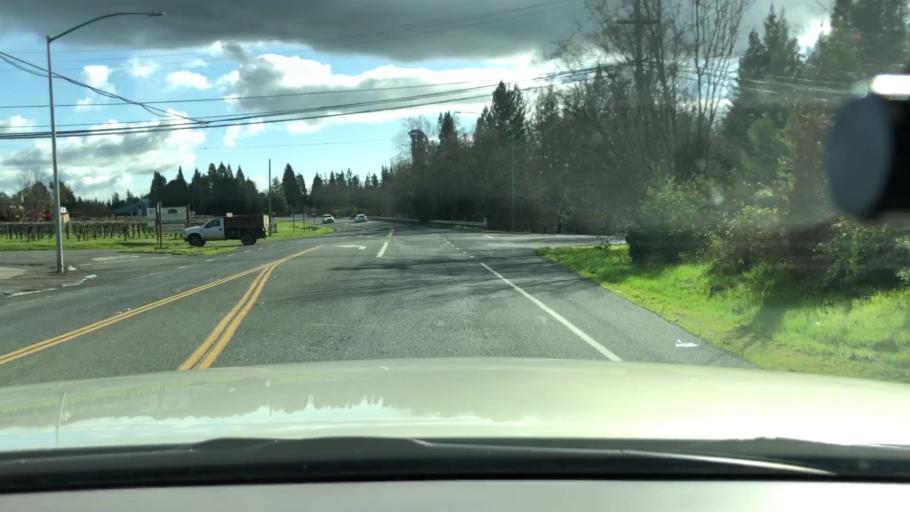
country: US
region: California
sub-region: Sonoma County
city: Graton
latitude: 38.4464
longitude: -122.8667
